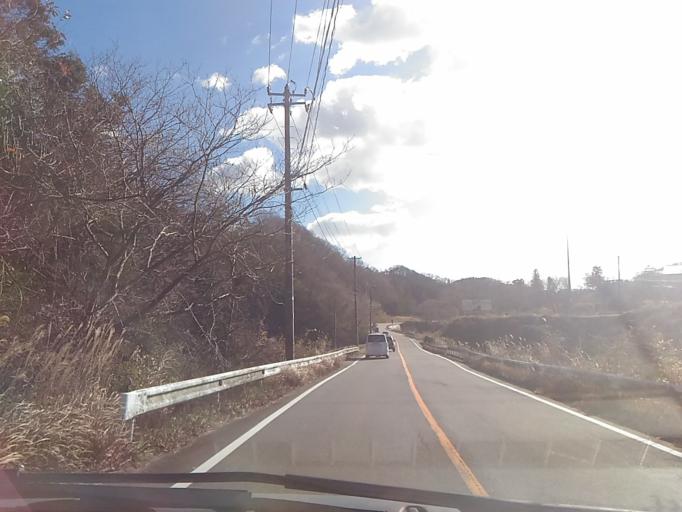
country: JP
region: Fukushima
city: Iwaki
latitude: 37.0077
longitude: 140.7824
